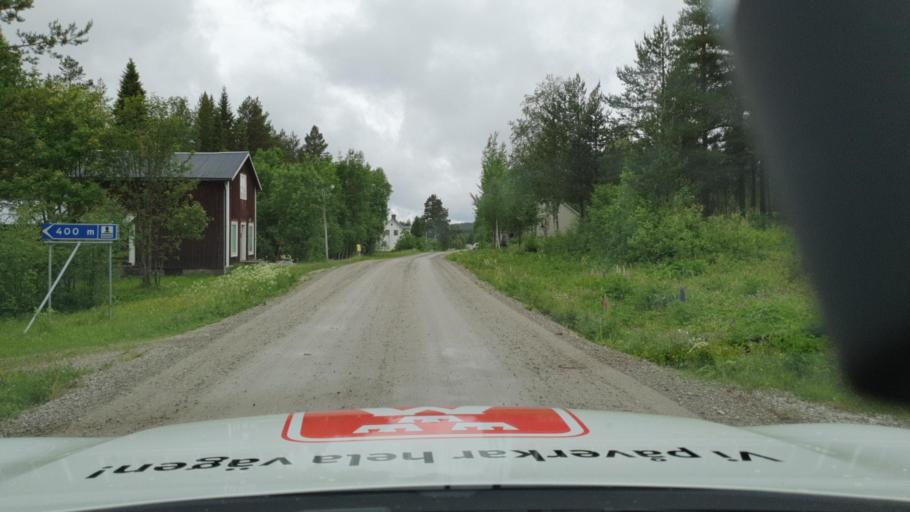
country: SE
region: Vaesterbotten
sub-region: Dorotea Kommun
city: Dorotea
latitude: 64.0164
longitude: 16.7948
